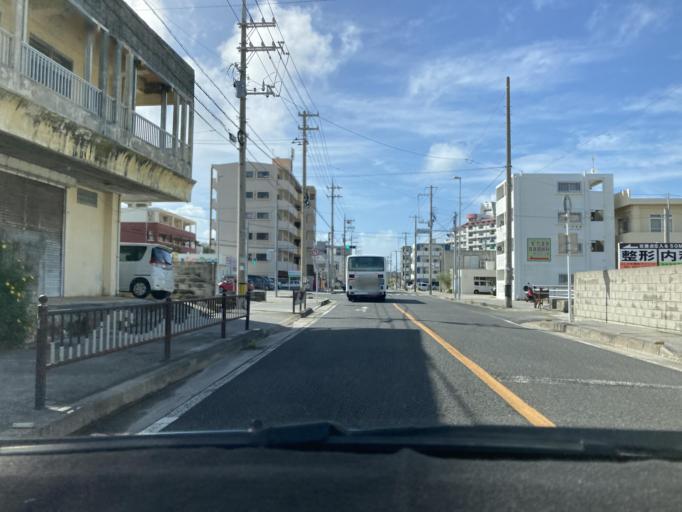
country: JP
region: Okinawa
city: Itoman
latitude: 26.1221
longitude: 127.6697
